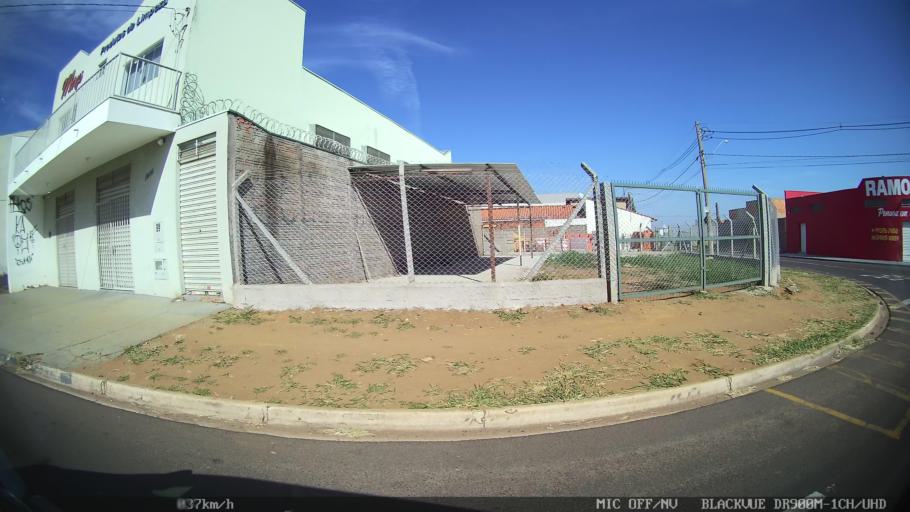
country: BR
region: Sao Paulo
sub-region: Franca
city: Franca
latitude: -20.5085
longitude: -47.4252
